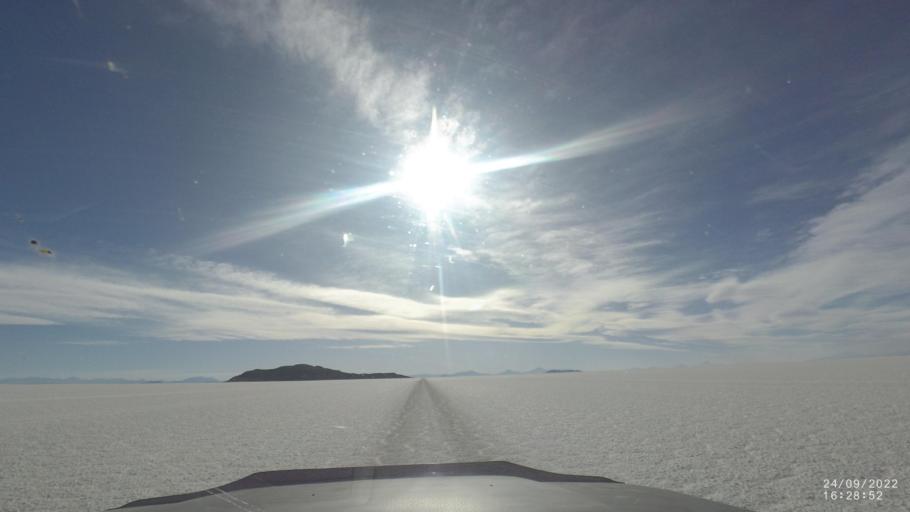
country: BO
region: Potosi
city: Colchani
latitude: -20.2411
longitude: -67.6062
